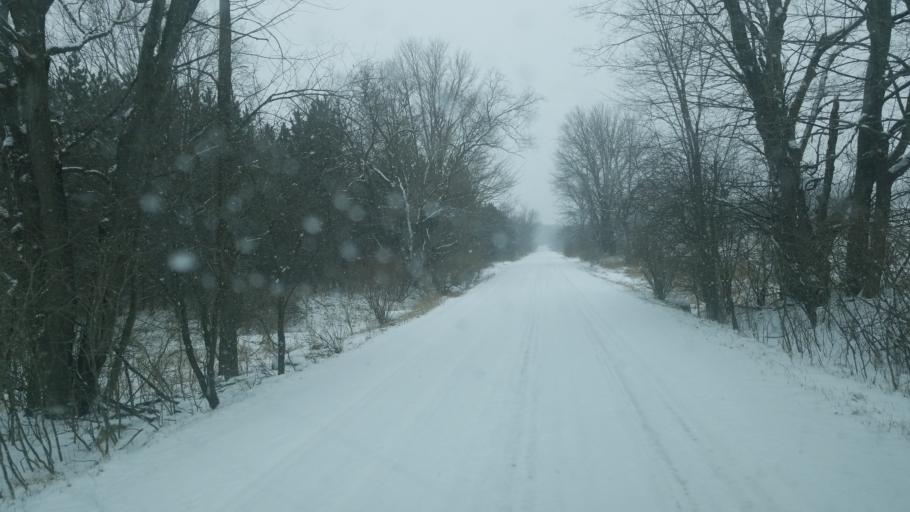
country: US
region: Michigan
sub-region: Osceola County
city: Reed City
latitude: 43.8366
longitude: -85.4141
